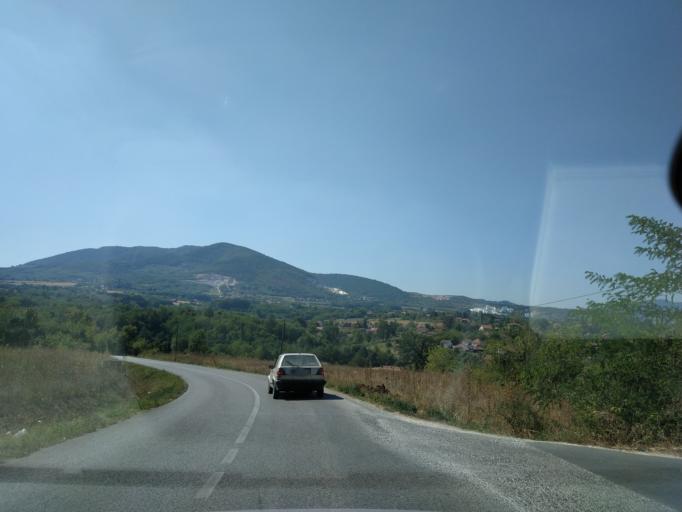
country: RS
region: Central Serbia
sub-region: Sumadijski Okrug
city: Topola
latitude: 44.2765
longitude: 20.6272
